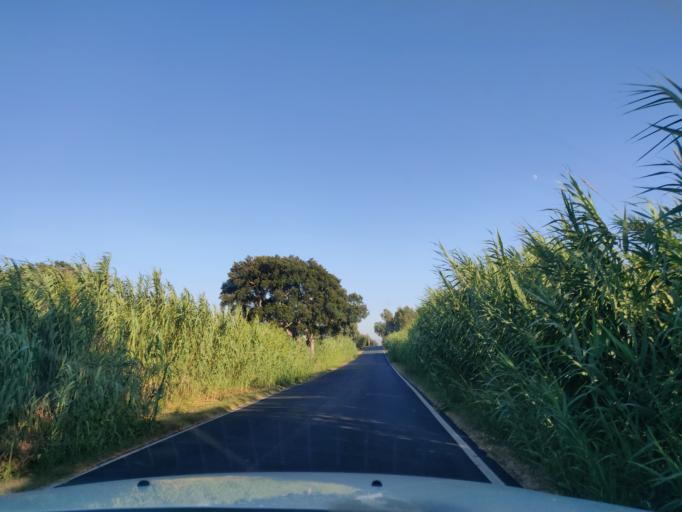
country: IT
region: Latium
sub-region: Provincia di Viterbo
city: Montalto di Castro
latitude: 42.2942
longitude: 11.6524
